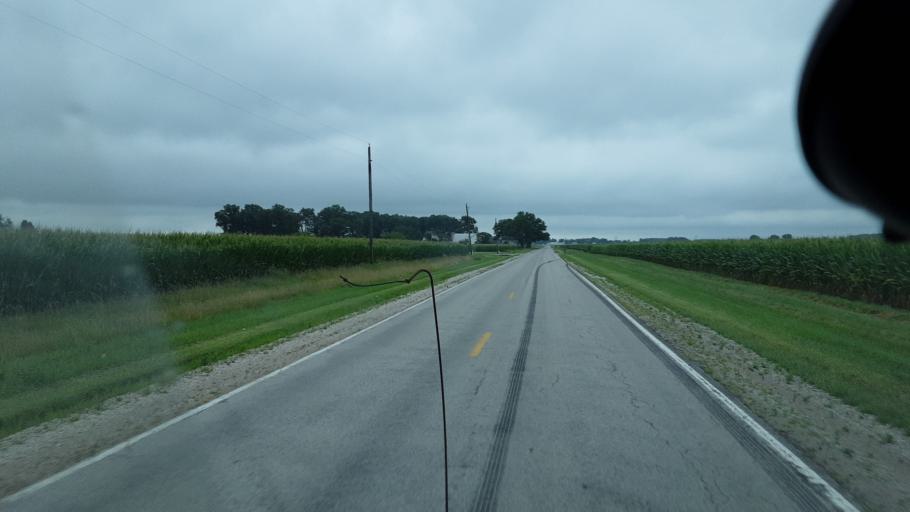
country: US
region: Indiana
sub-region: Wells County
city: Bluffton
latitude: 40.8003
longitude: -85.0908
